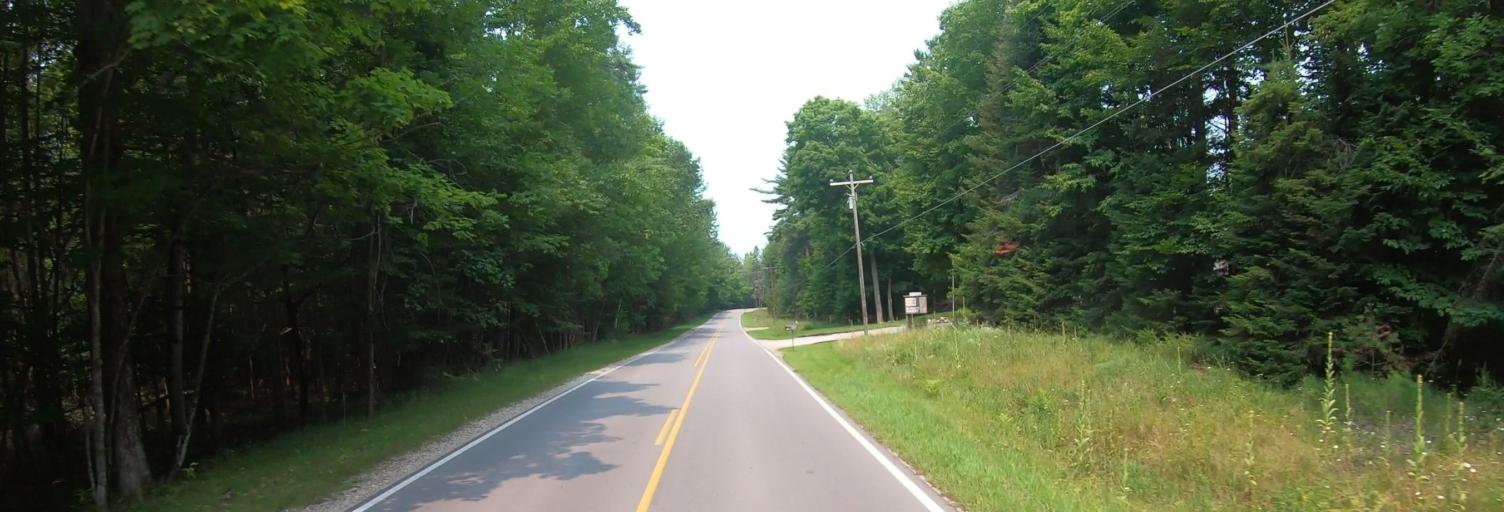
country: CA
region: Ontario
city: Thessalon
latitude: 46.0238
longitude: -83.7330
